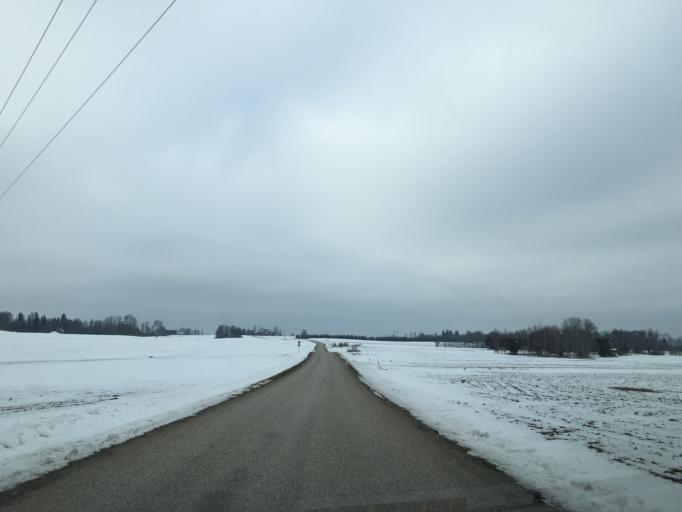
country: EE
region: Tartu
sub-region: Elva linn
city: Elva
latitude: 58.1177
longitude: 26.2387
